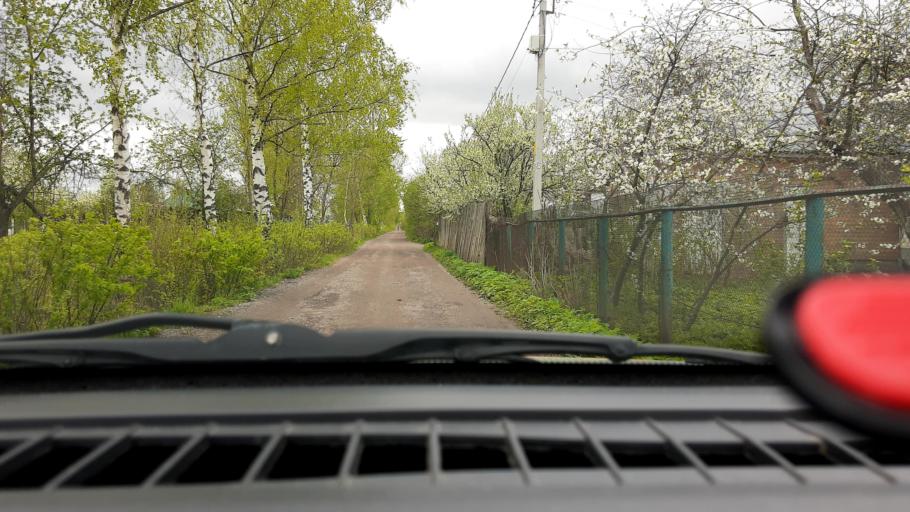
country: RU
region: Nizjnij Novgorod
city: Gorbatovka
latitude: 56.2422
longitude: 43.8130
